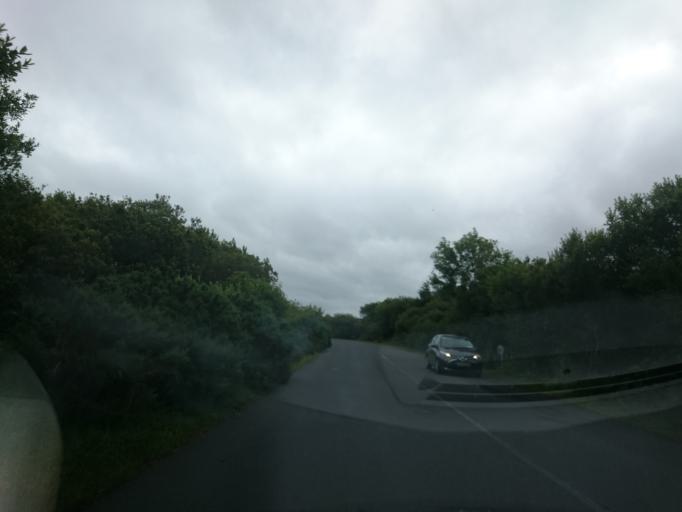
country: IE
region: Connaught
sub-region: County Galway
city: Clifden
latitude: 53.5509
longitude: -9.9517
